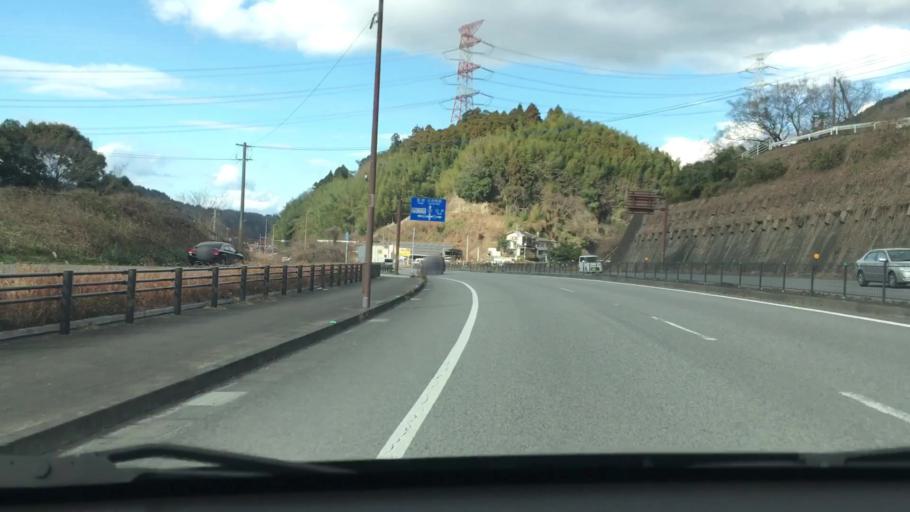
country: JP
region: Oita
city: Oita
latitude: 33.1112
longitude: 131.6567
